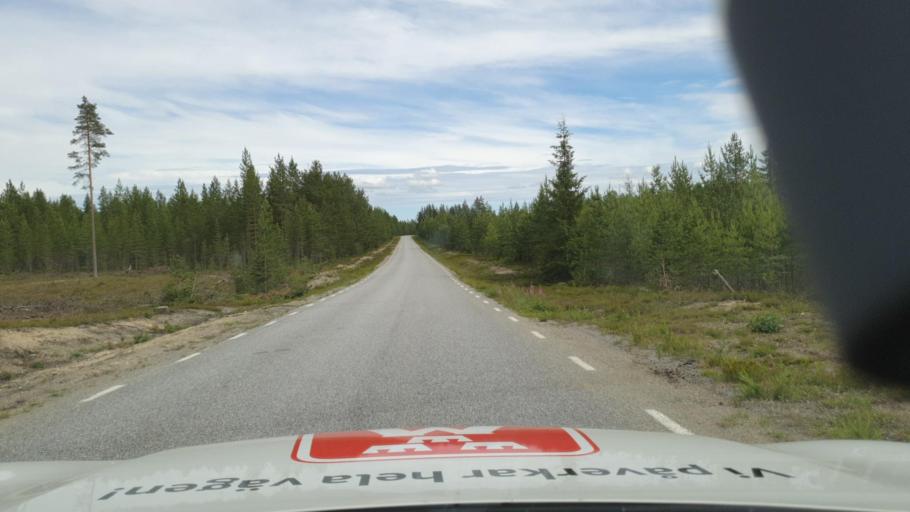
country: SE
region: Vaesterbotten
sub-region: Skelleftea Kommun
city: Burtraesk
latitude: 64.5036
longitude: 20.8232
